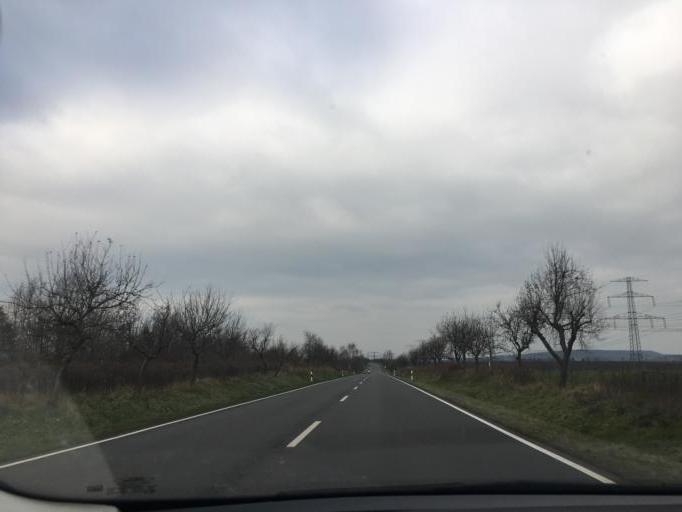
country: DE
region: Saxony
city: Kitzscher
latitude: 51.1377
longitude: 12.5489
